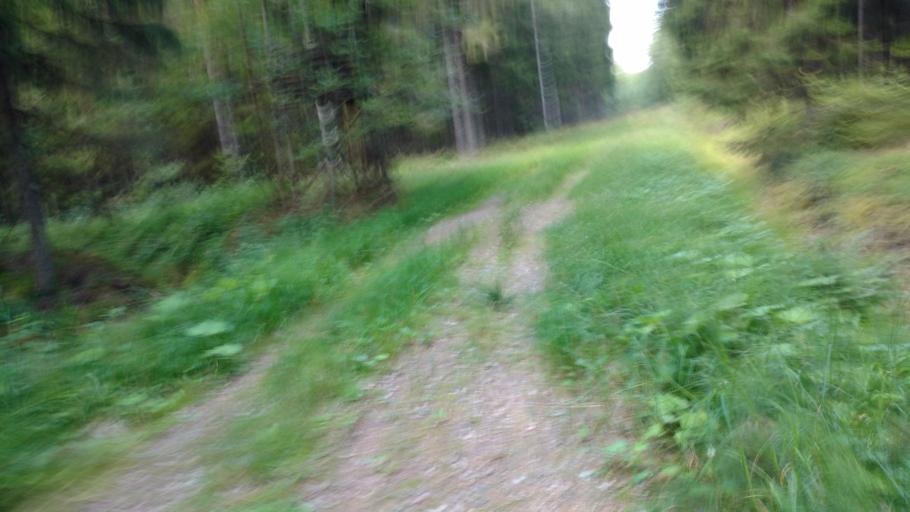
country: FI
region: Varsinais-Suomi
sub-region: Salo
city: Pertteli
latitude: 60.3924
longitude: 23.2289
